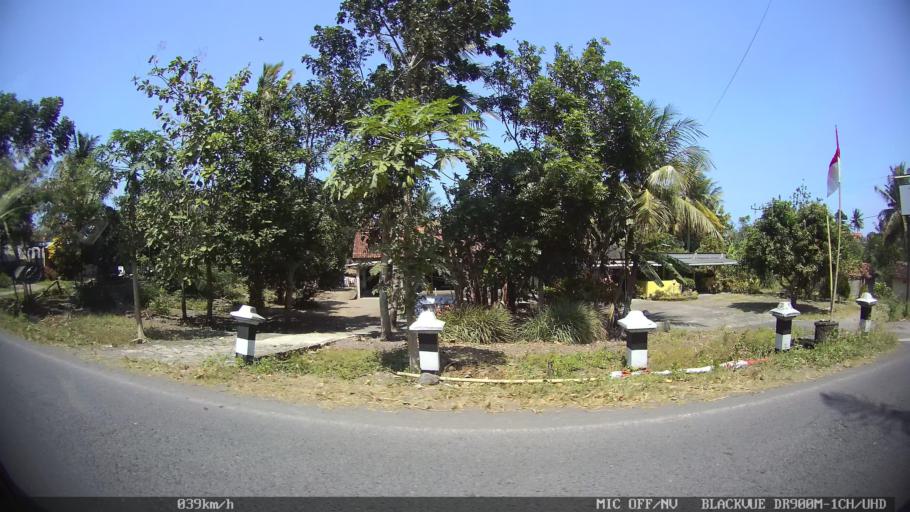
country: ID
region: Daerah Istimewa Yogyakarta
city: Srandakan
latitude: -7.9086
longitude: 110.0842
